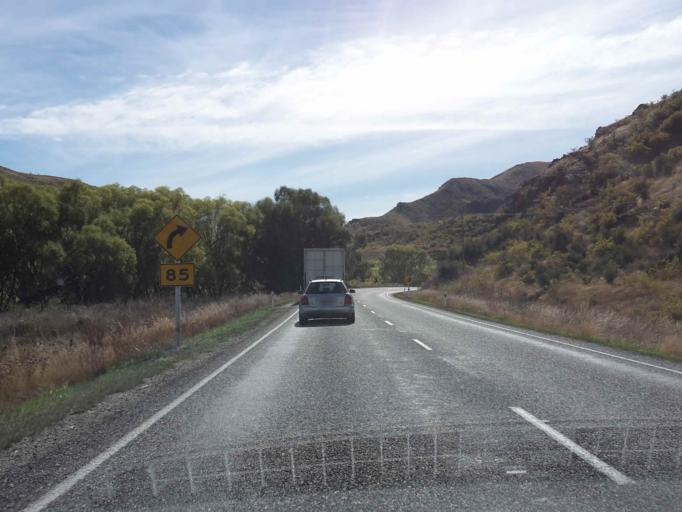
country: NZ
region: Otago
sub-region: Queenstown-Lakes District
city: Wanaka
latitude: -44.7447
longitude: 169.5094
